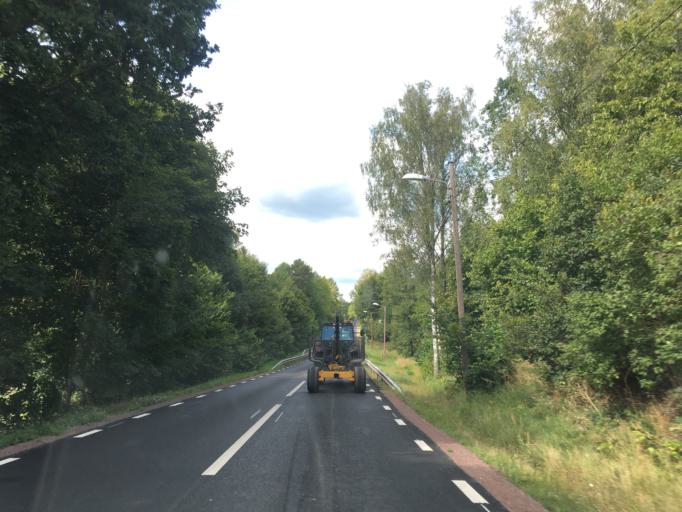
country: SE
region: Kalmar
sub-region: Kalmar Kommun
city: Trekanten
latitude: 56.8947
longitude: 16.0540
